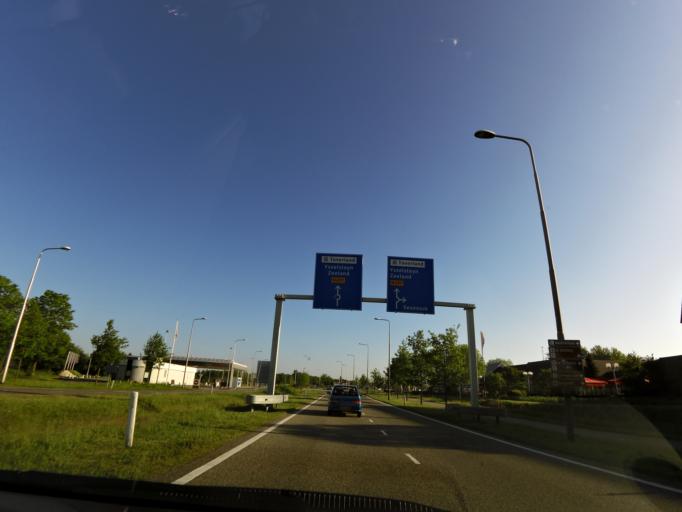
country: NL
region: Limburg
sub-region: Gemeente Peel en Maas
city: Maasbree
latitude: 51.3786
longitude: 5.9844
